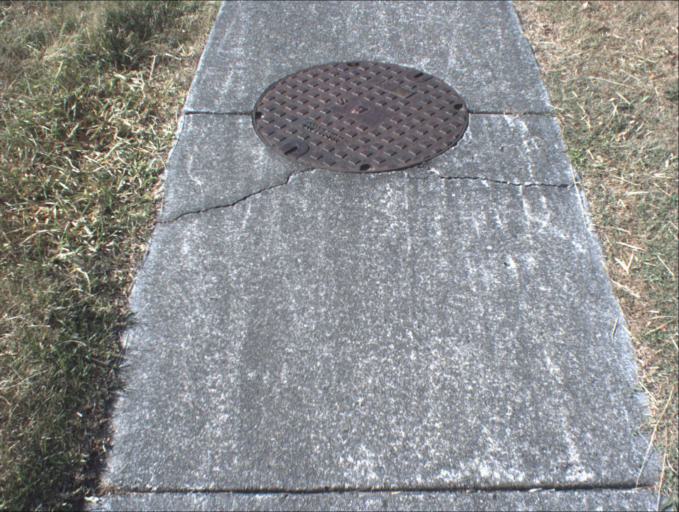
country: AU
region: Queensland
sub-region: Logan
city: Beenleigh
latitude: -27.6799
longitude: 153.1797
